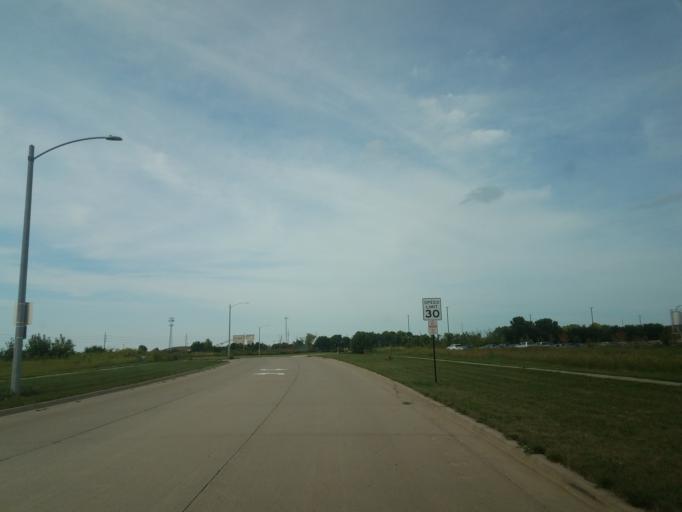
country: US
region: Illinois
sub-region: McLean County
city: Normal
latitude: 40.5280
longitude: -88.9488
